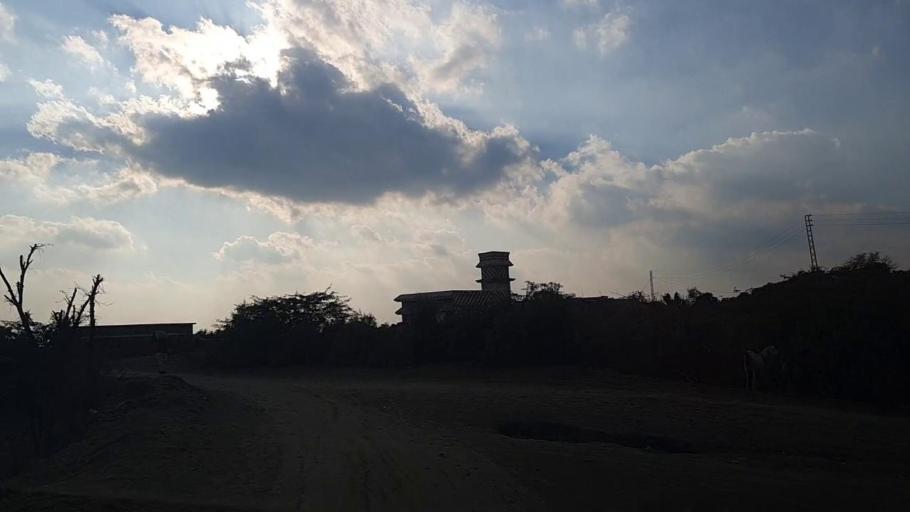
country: PK
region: Sindh
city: Tando Mittha Khan
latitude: 25.9434
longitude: 69.2501
